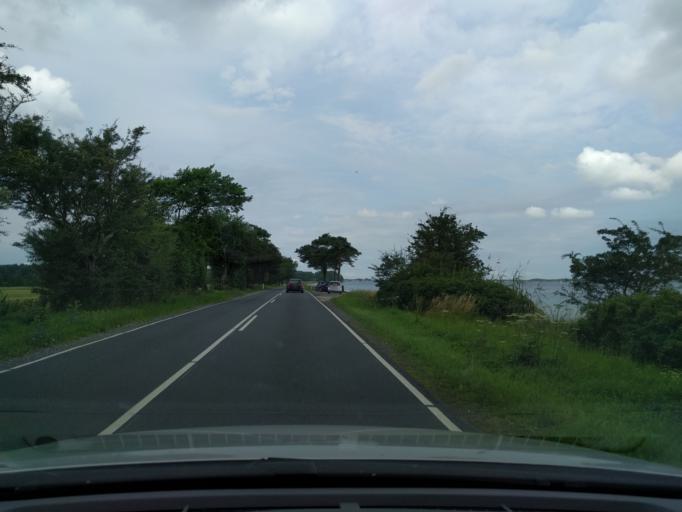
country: DK
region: South Denmark
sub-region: Kerteminde Kommune
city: Kerteminde
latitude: 55.4206
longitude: 10.7067
